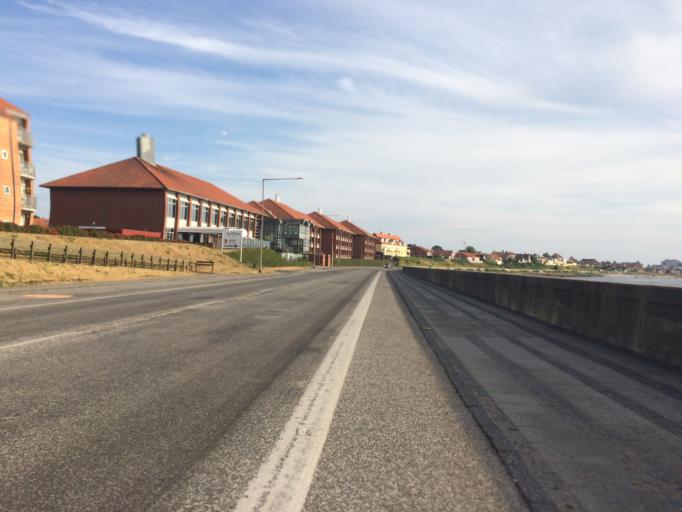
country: DK
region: Capital Region
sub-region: Bornholm Kommune
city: Ronne
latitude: 55.1088
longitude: 14.7005
